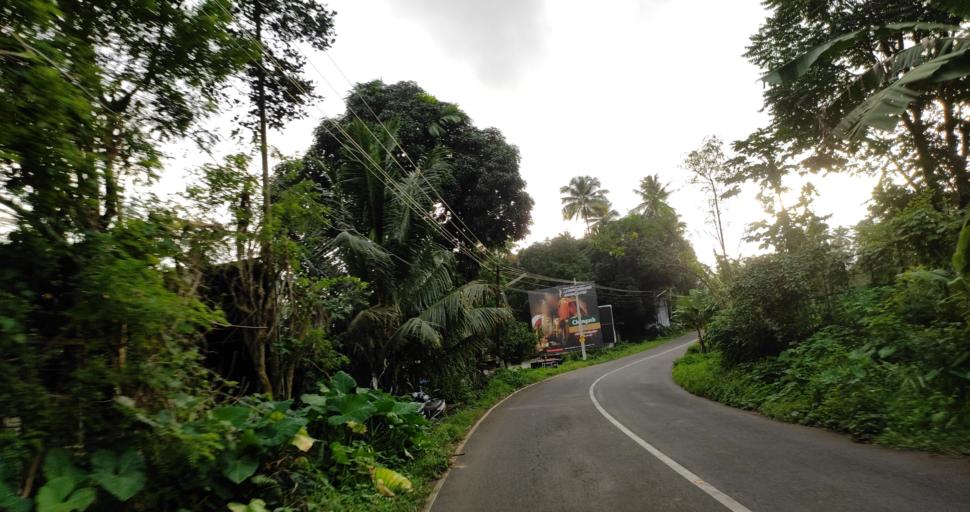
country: IN
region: Kerala
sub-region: Thrissur District
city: Kizhake Chalakudi
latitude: 10.2992
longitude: 76.4327
